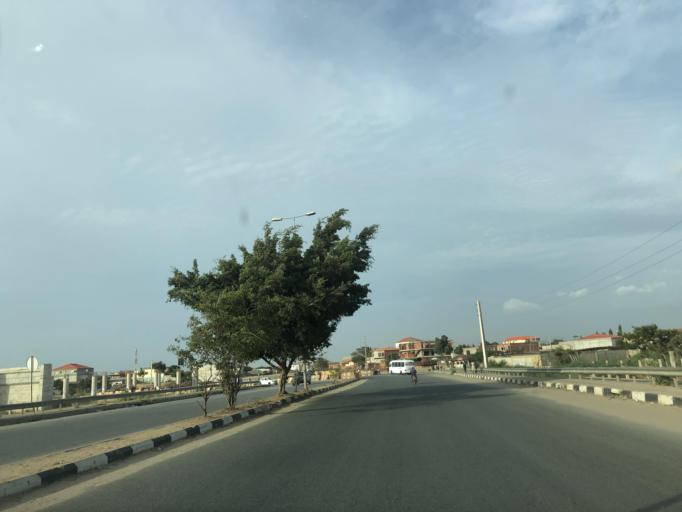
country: AO
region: Luanda
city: Luanda
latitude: -8.9303
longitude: 13.3025
